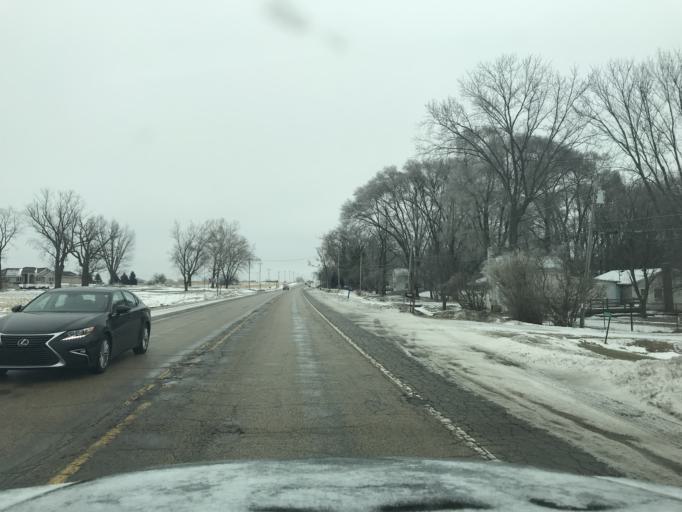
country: US
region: Wisconsin
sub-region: Dane County
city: Cottage Grove
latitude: 43.0897
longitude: -89.2369
